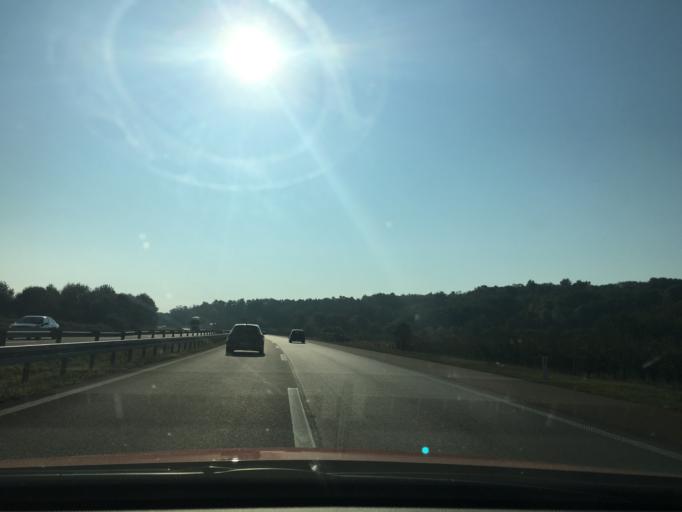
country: RS
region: Central Serbia
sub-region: Podunavski Okrug
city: Smederevo
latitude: 44.5824
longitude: 20.8705
